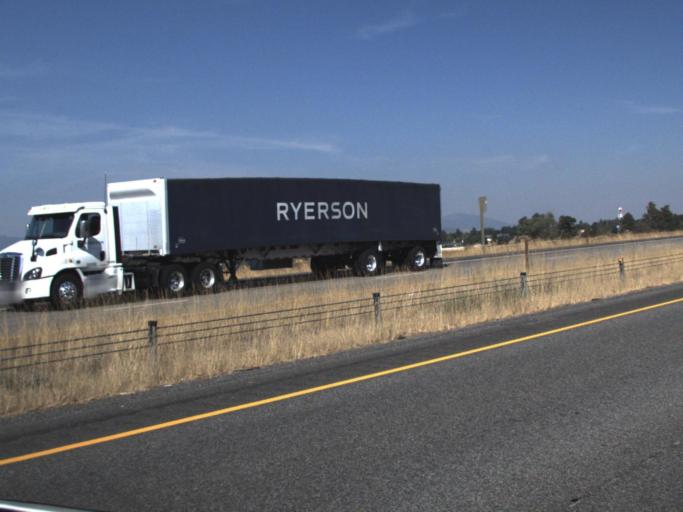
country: US
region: Washington
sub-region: Spokane County
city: Liberty Lake
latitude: 47.6791
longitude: -117.0996
